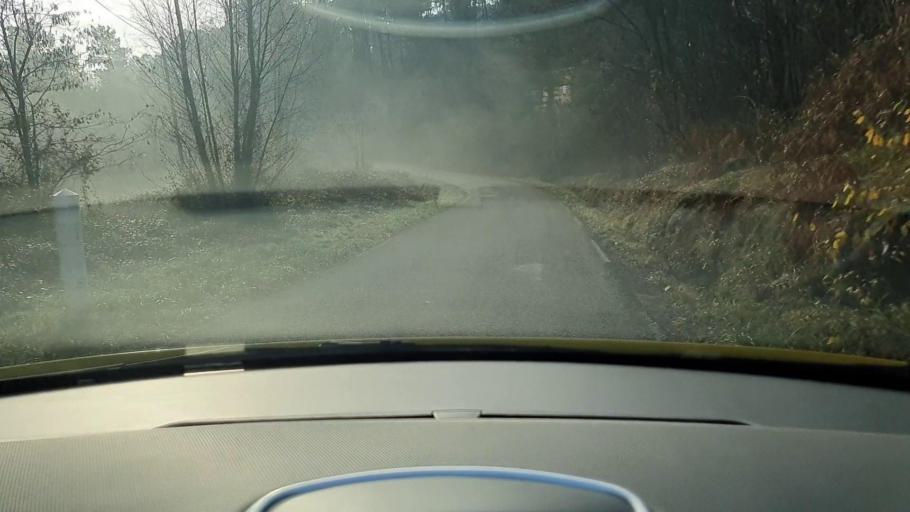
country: FR
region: Languedoc-Roussillon
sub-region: Departement du Gard
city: Branoux-les-Taillades
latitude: 44.2967
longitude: 4.0042
